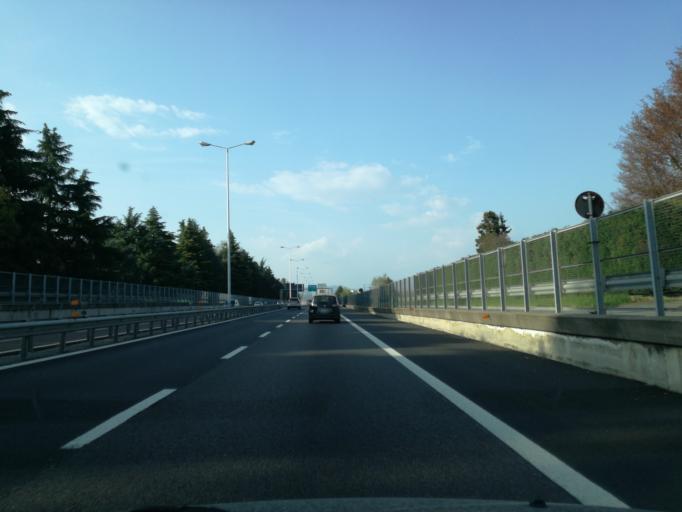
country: IT
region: Lombardy
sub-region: Provincia di Monza e Brianza
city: Velasca
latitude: 45.6255
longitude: 9.3616
